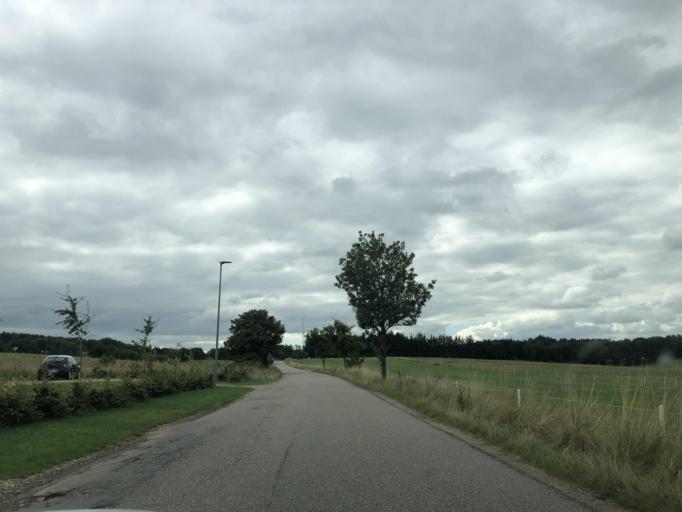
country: DK
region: North Denmark
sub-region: Alborg Kommune
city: Svenstrup
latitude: 56.9388
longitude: 9.8087
